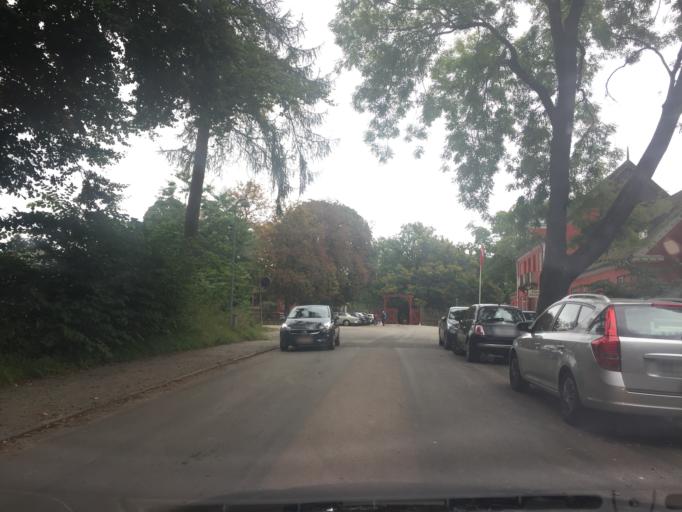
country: DK
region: Capital Region
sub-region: Lyngby-Tarbaek Kommune
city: Kongens Lyngby
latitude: 55.7749
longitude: 12.5435
